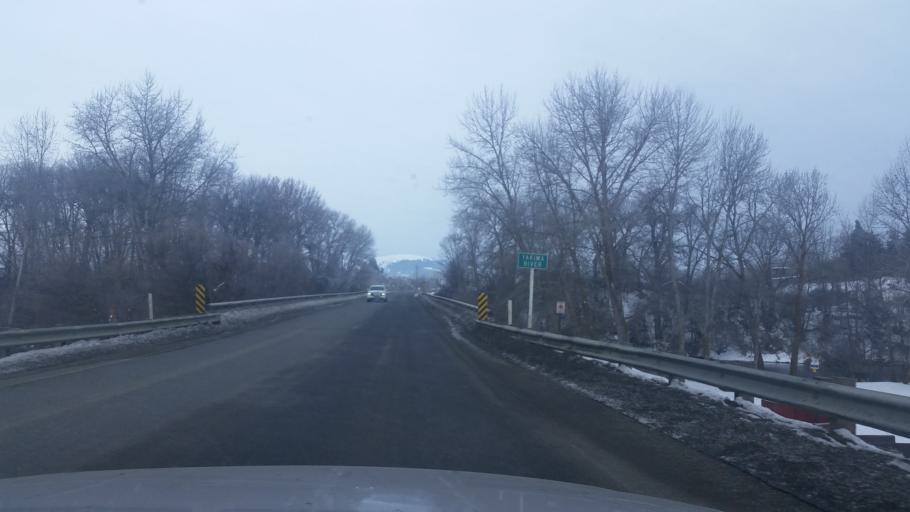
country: US
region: Washington
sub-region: Kittitas County
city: Ellensburg
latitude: 47.0059
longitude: -120.5952
